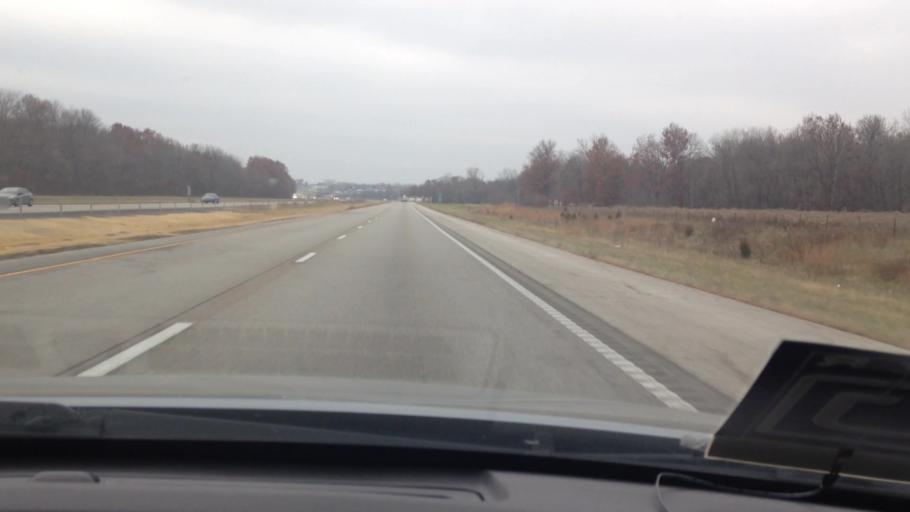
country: US
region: Missouri
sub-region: Cass County
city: Peculiar
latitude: 38.6925
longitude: -94.4280
